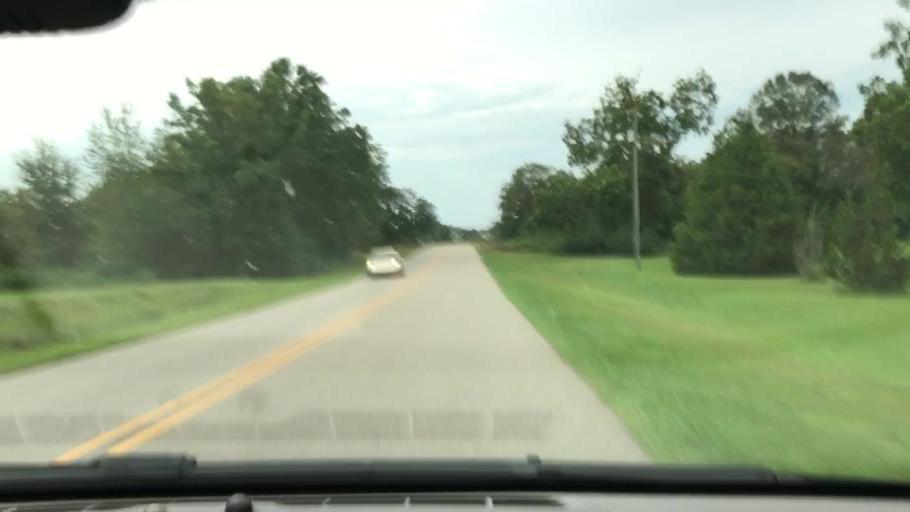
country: US
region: Alabama
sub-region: Houston County
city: Ashford
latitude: 31.2514
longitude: -85.1676
